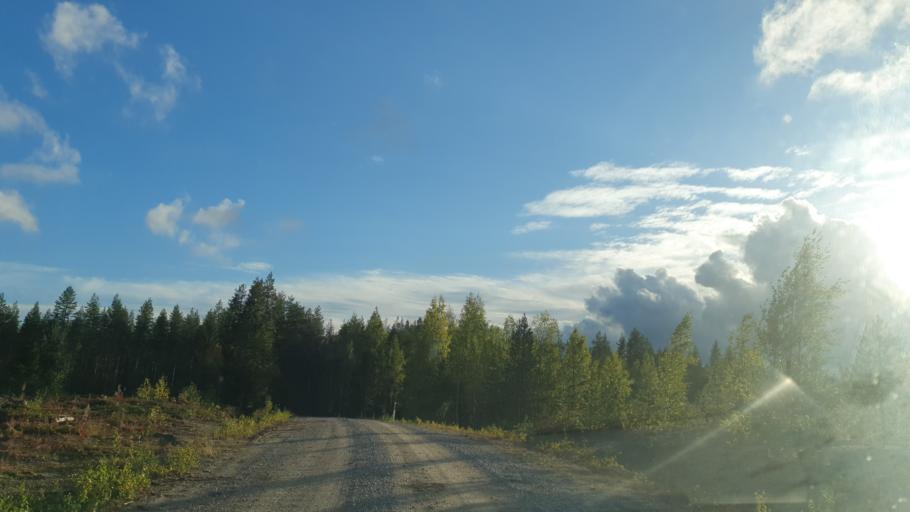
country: FI
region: Kainuu
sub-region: Kehys-Kainuu
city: Kuhmo
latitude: 64.3374
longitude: 29.9628
